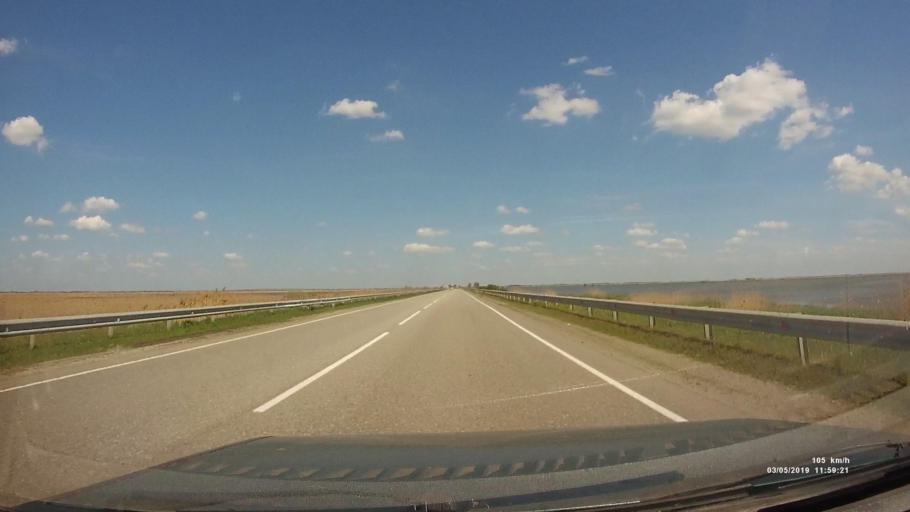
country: RU
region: Rostov
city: Bagayevskaya
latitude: 47.2337
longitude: 40.3295
